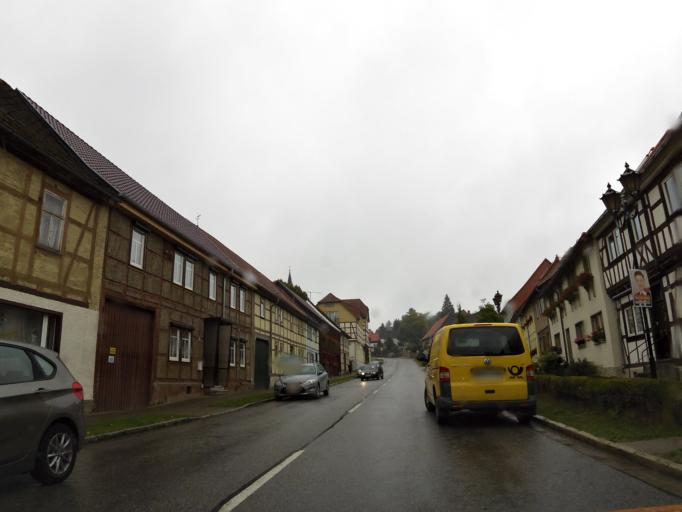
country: DE
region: Saxony-Anhalt
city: Stolberg
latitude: 51.6438
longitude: 10.9791
